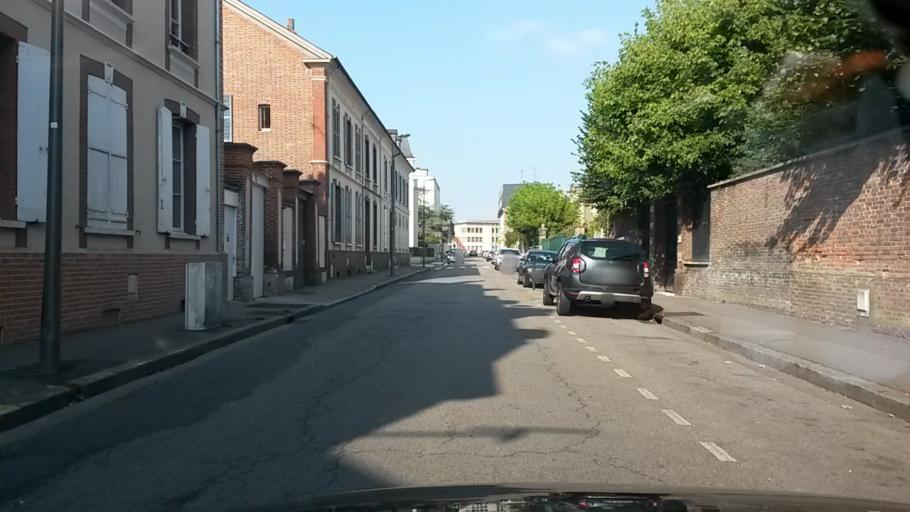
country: FR
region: Haute-Normandie
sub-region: Departement de l'Eure
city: Evreux
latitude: 49.0221
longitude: 1.1437
